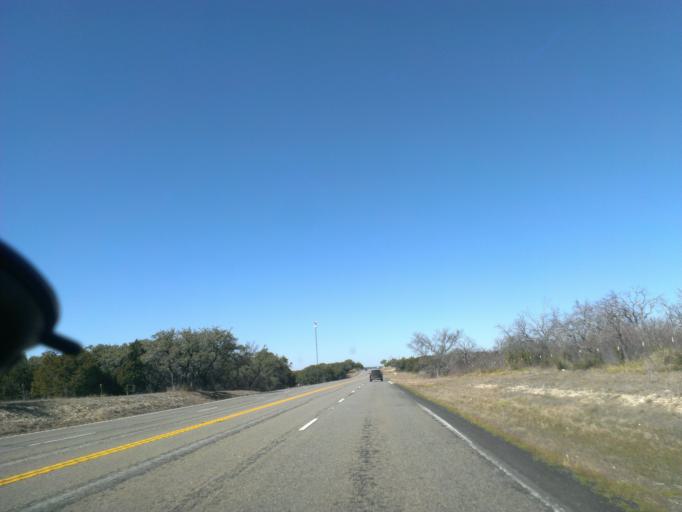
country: US
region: Texas
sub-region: Lampasas County
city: Kempner
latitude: 30.9165
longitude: -97.9790
